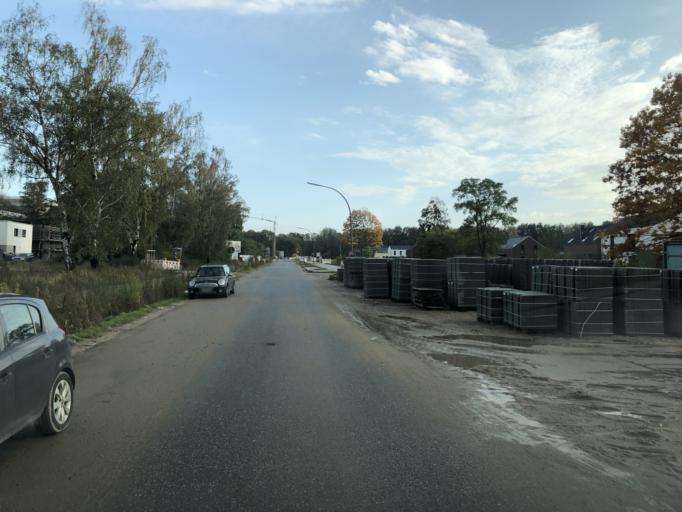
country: DE
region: Lower Saxony
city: Neu Wulmstorf
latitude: 53.4664
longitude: 9.8107
